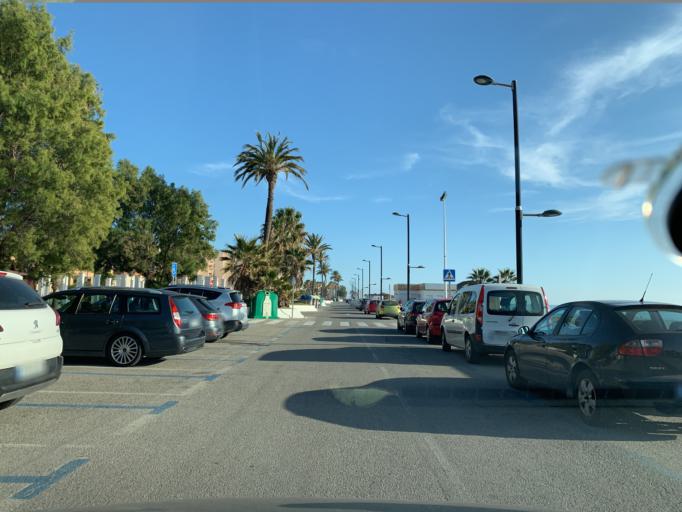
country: ES
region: Andalusia
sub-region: Provincia de Granada
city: Salobrena
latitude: 36.7320
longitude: -3.5874
